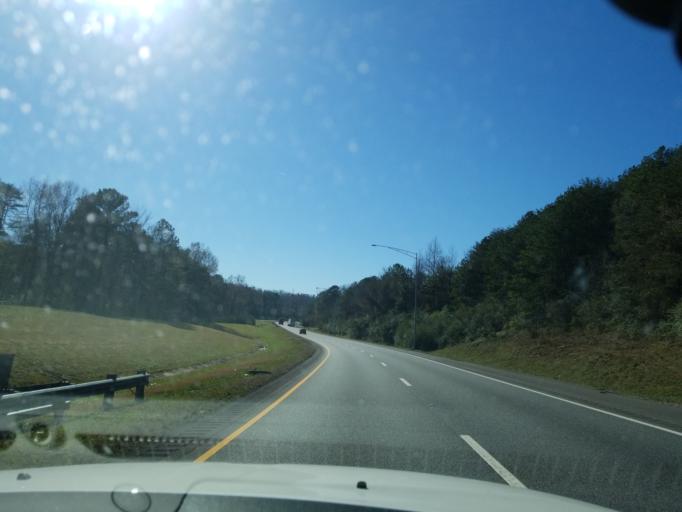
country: US
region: Alabama
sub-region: Jefferson County
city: Bessemer
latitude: 33.3401
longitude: -87.0336
